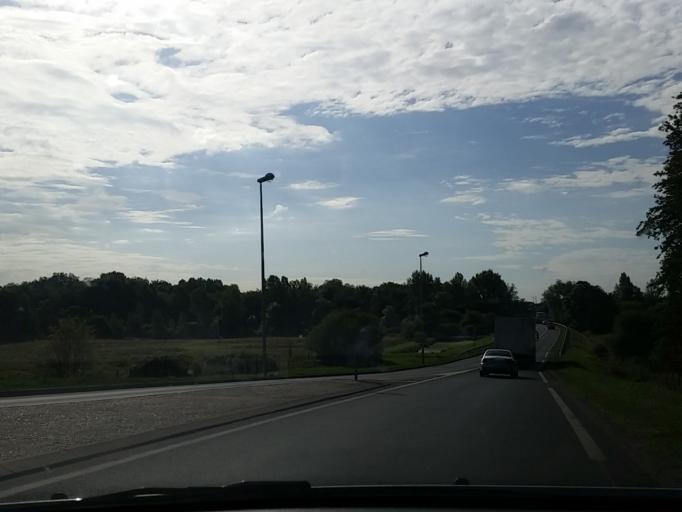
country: FR
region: Centre
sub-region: Departement du Loir-et-Cher
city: Romorantin-Lanthenay
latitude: 47.3499
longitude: 1.7239
